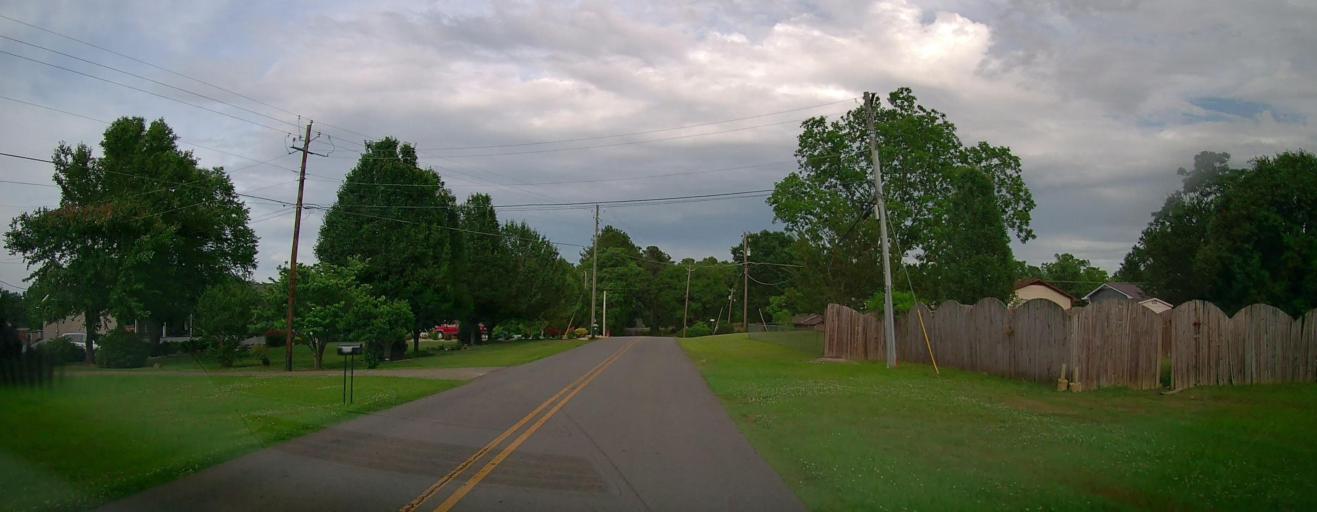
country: US
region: Alabama
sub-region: Calhoun County
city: Oxford
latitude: 33.5857
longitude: -85.8128
